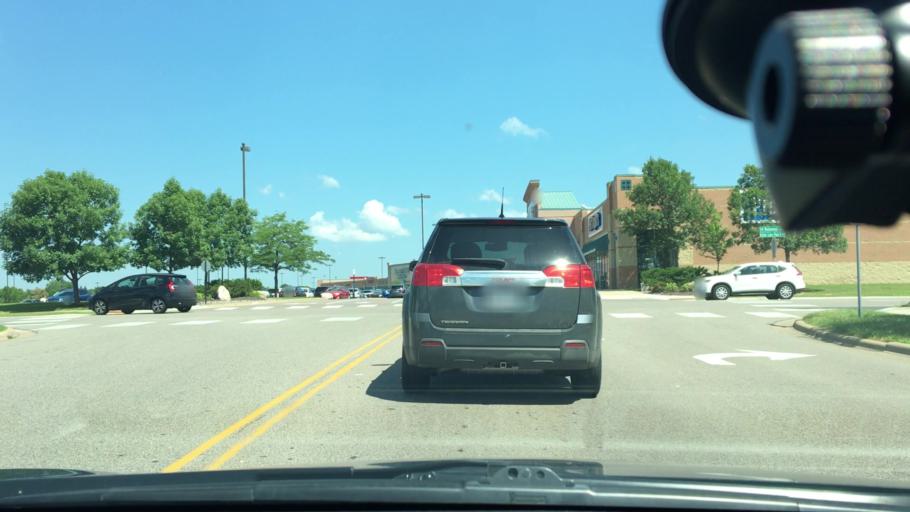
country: US
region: Minnesota
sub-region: Hennepin County
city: Maple Grove
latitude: 45.0978
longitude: -93.4474
